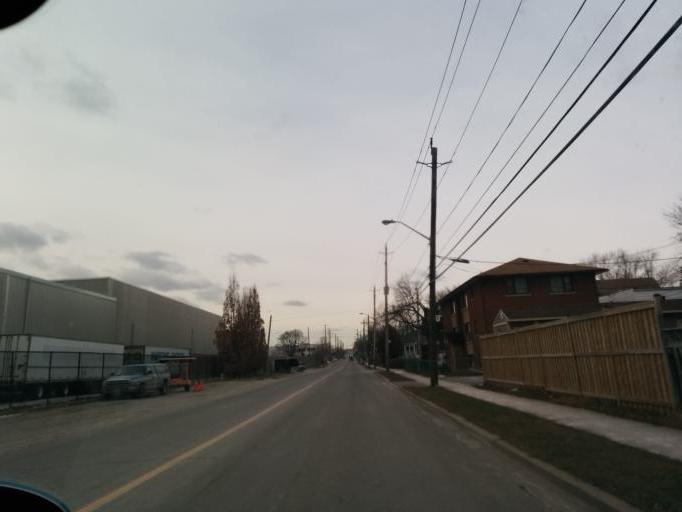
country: CA
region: Ontario
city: Etobicoke
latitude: 43.6058
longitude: -79.4993
